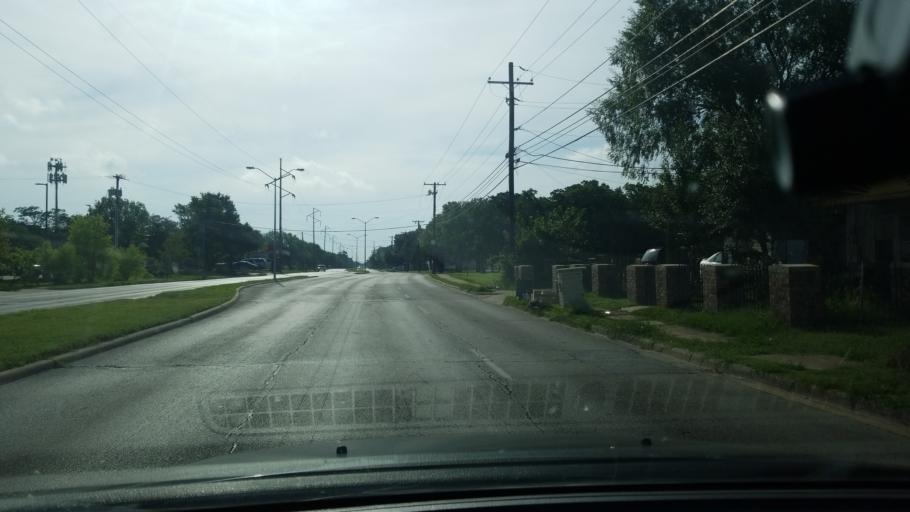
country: US
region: Texas
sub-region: Dallas County
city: Balch Springs
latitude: 32.7196
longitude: -96.6639
